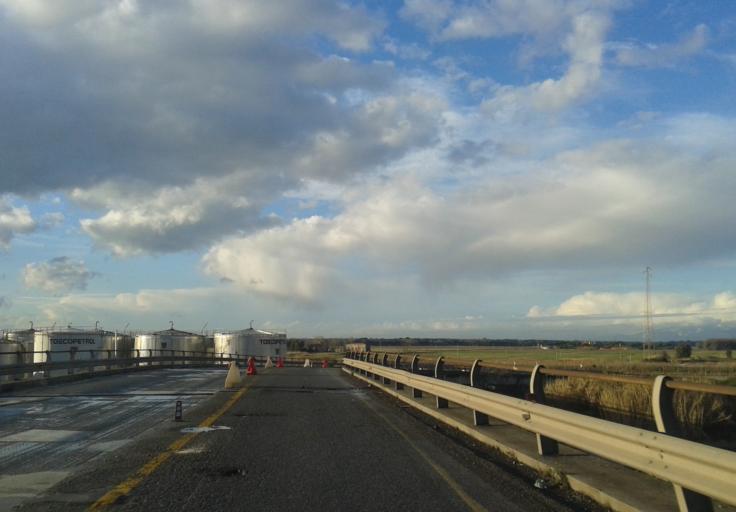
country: IT
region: Tuscany
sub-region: Provincia di Livorno
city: Livorno
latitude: 43.5876
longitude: 10.3233
